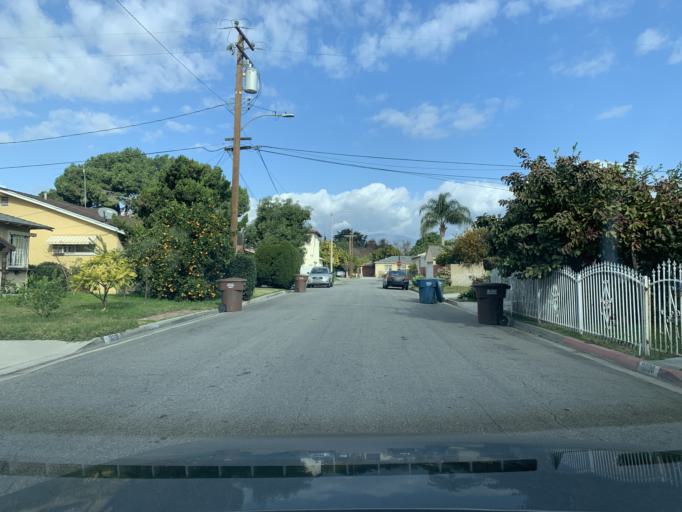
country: US
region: California
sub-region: Los Angeles County
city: South El Monte
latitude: 34.0665
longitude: -118.0466
